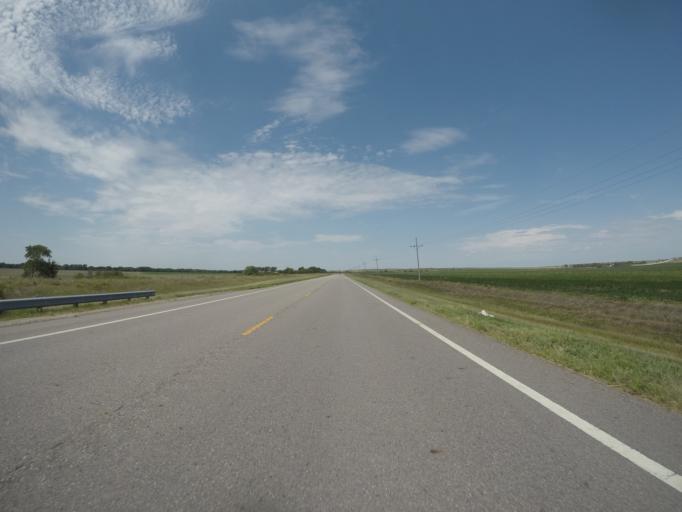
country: US
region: Kansas
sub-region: Rooks County
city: Stockton
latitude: 39.4541
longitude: -99.1123
